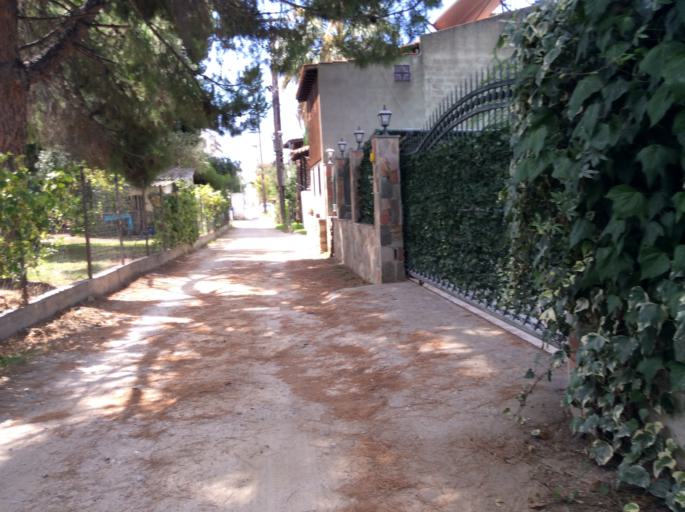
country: GR
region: Central Macedonia
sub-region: Nomos Chalkidikis
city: Sykia
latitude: 39.9896
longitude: 23.9006
